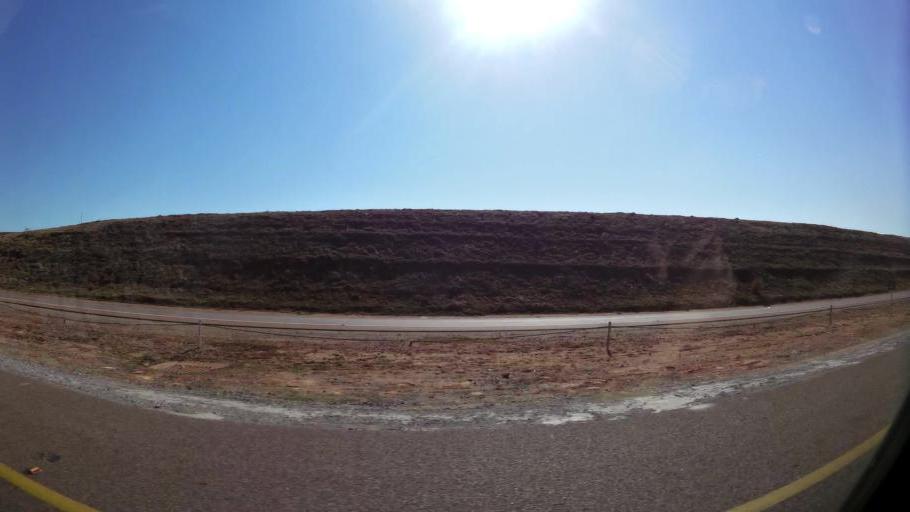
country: ZA
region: Gauteng
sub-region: City of Tshwane Metropolitan Municipality
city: Pretoria
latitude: -25.6547
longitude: 28.1107
